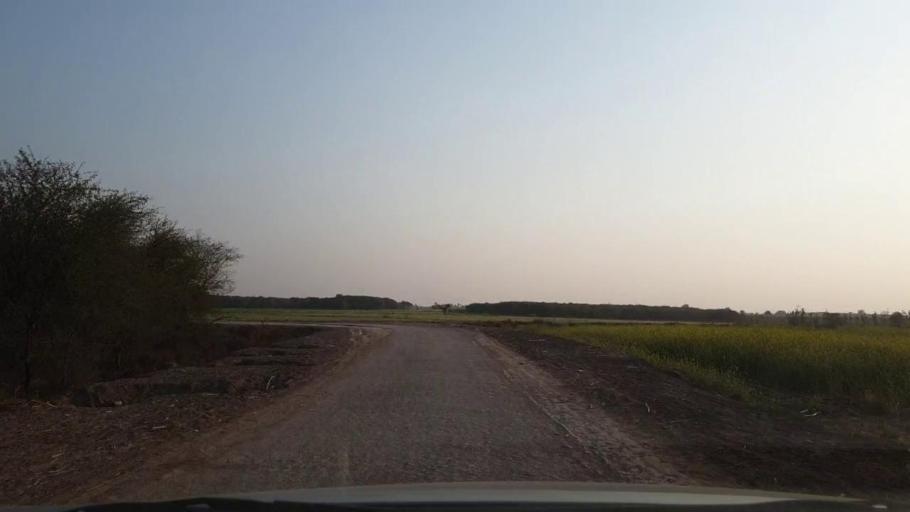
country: PK
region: Sindh
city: Tando Adam
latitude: 25.7132
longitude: 68.5973
